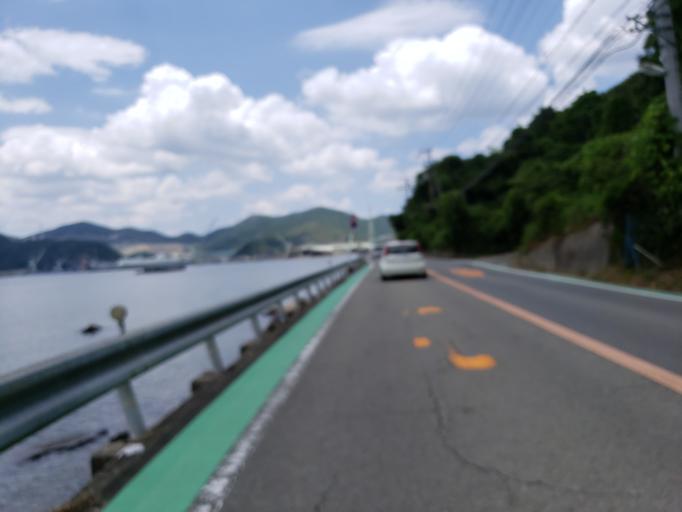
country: JP
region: Hyogo
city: Aioi
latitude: 34.7877
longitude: 134.4752
